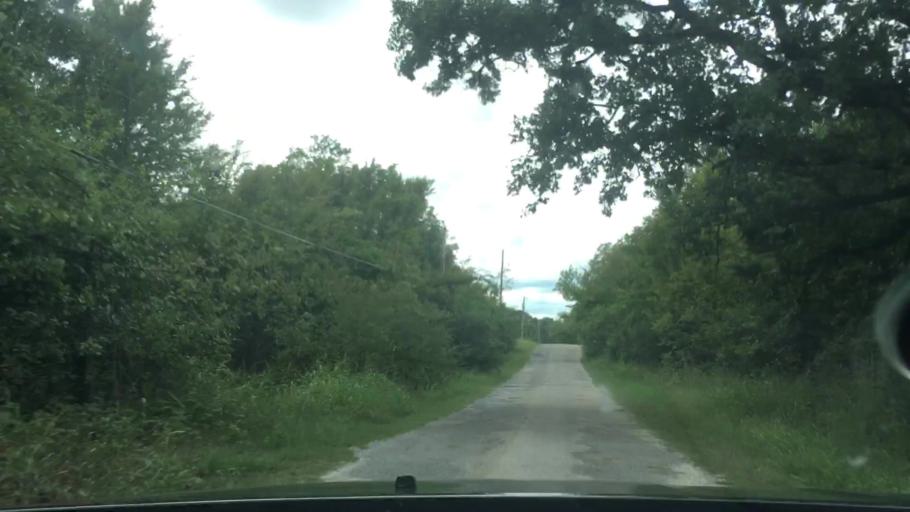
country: US
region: Oklahoma
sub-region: Pontotoc County
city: Ada
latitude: 34.7526
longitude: -96.6495
